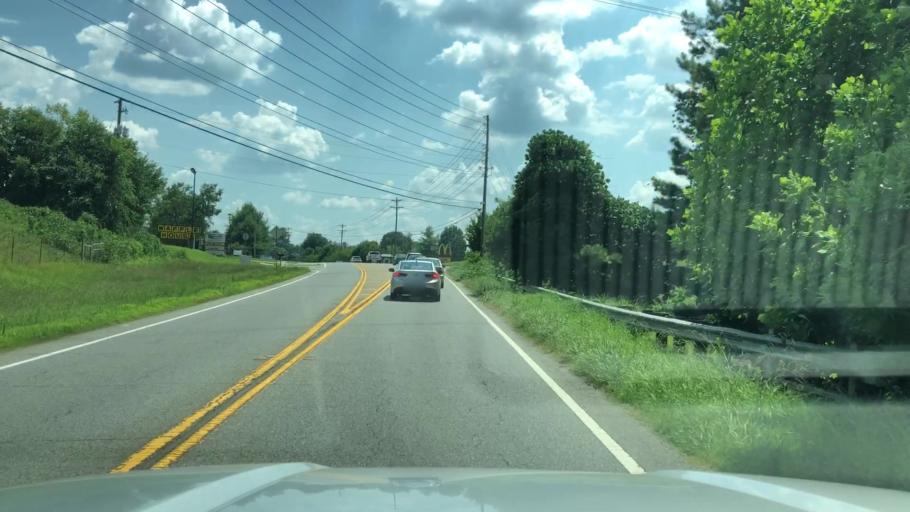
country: US
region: Georgia
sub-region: Cobb County
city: Acworth
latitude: 34.0010
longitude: -84.7036
